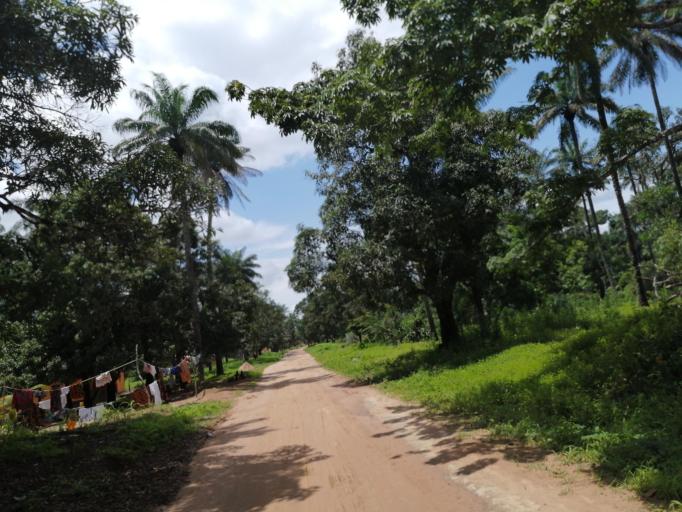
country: SL
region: Northern Province
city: Konakridee
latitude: 8.7727
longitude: -13.1383
